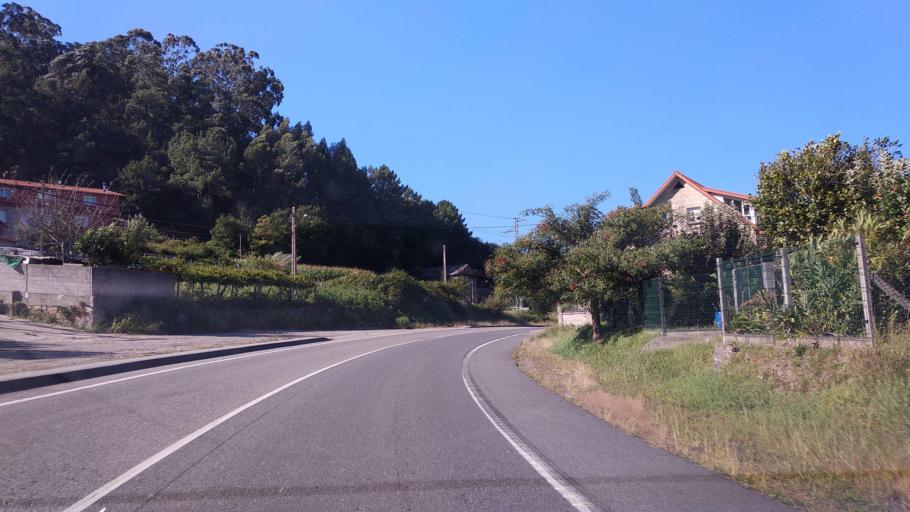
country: ES
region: Galicia
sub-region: Provincia de Pontevedra
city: Redondela
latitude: 42.3100
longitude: -8.6628
